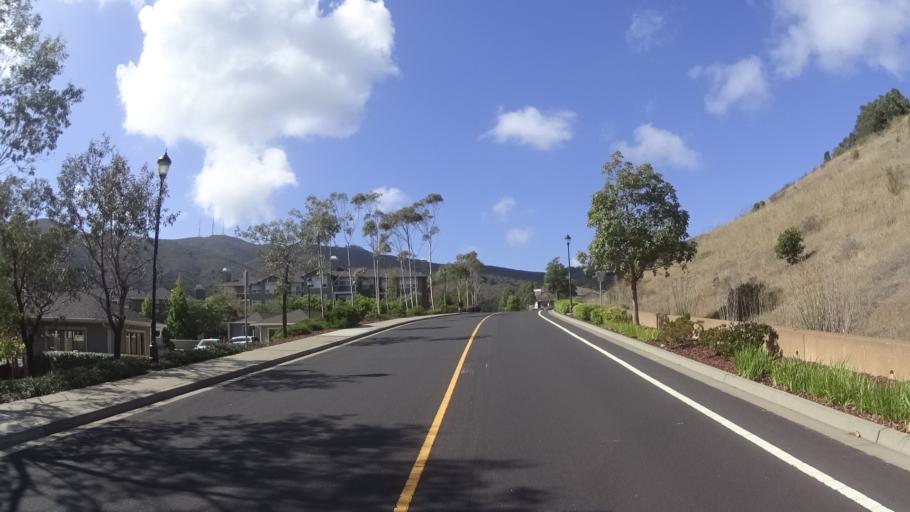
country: US
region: California
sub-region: San Mateo County
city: Brisbane
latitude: 37.6929
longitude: -122.4161
